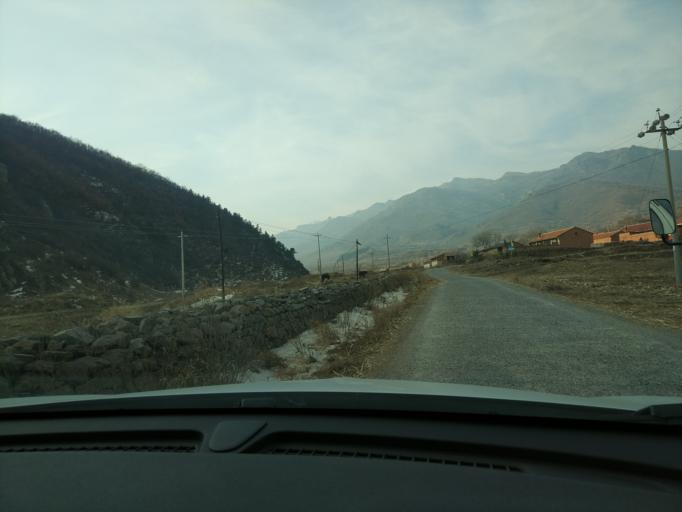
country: CN
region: Hebei
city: Xiwanzi
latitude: 40.8246
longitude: 115.5126
